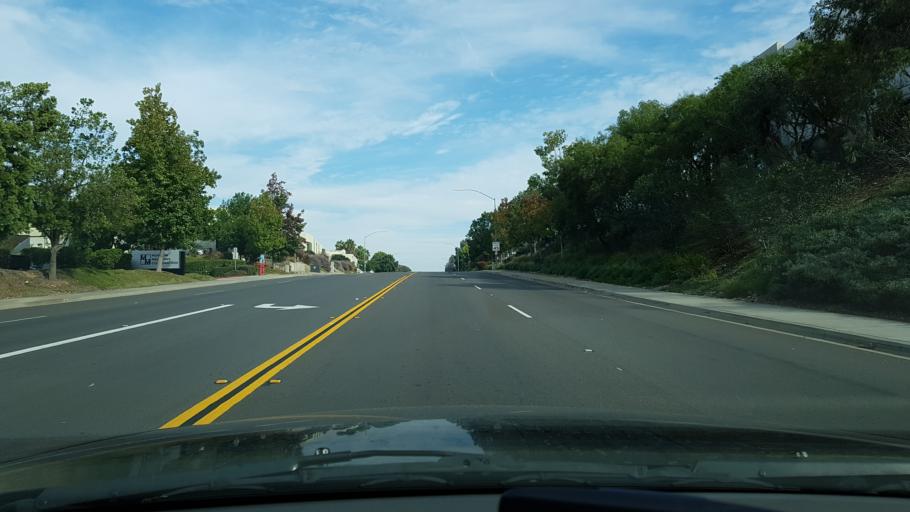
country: US
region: California
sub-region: San Diego County
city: Poway
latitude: 32.9351
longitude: -117.0459
